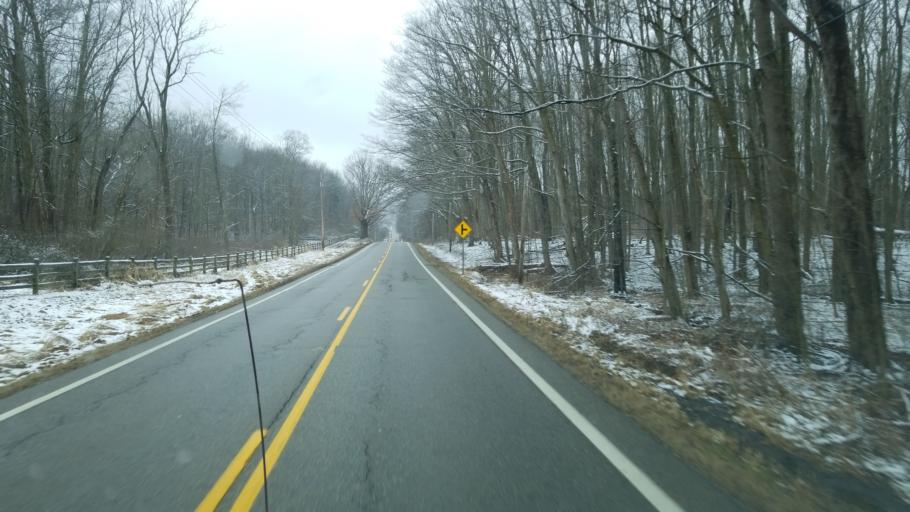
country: US
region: Ohio
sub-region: Portage County
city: Hiram
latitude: 41.3098
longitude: -81.1179
